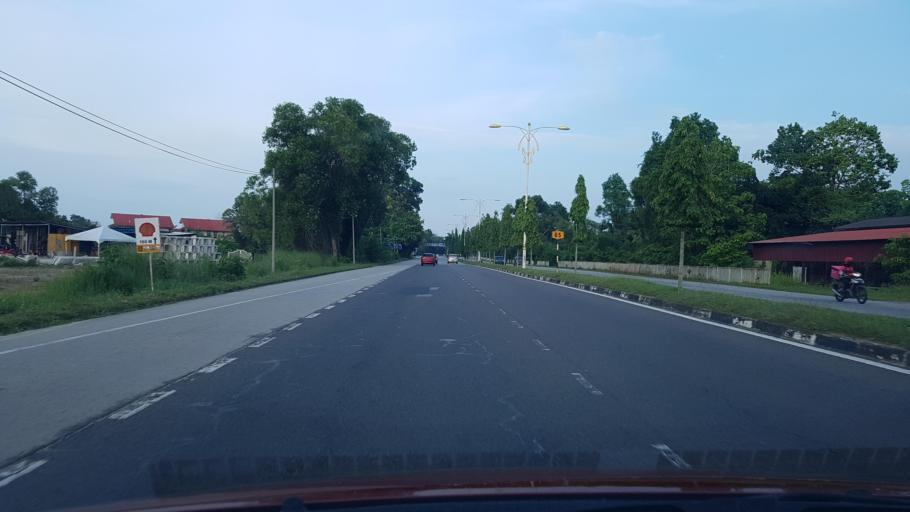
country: MY
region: Terengganu
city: Kuala Terengganu
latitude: 5.3393
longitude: 103.1068
